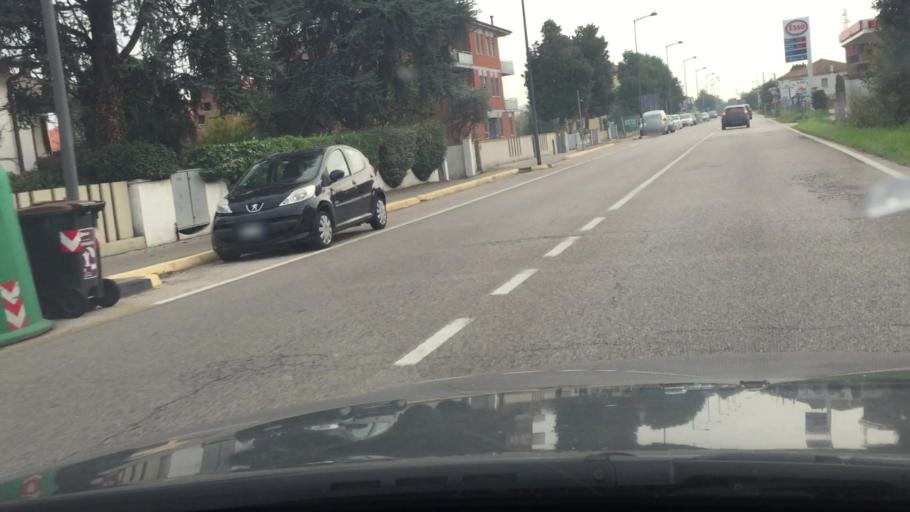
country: IT
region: Emilia-Romagna
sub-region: Provincia di Ferrara
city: Ferrara
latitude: 44.8418
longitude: 11.5839
